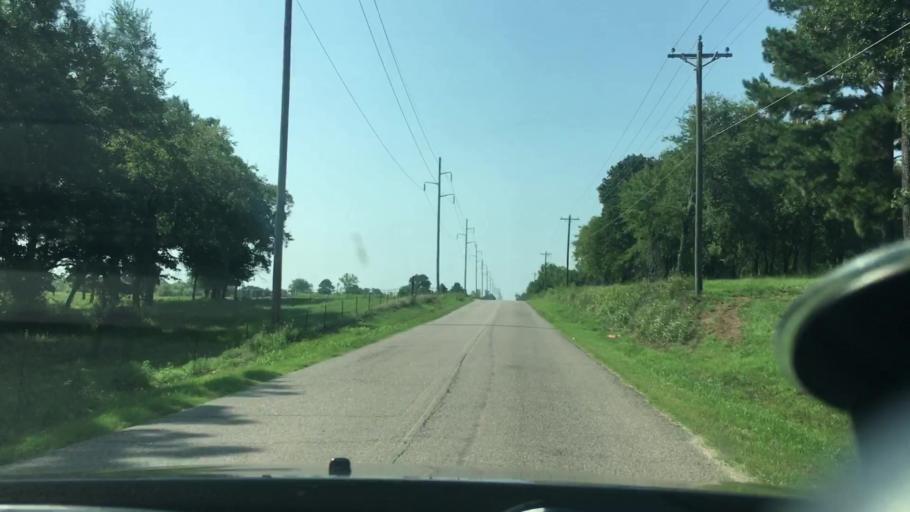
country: US
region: Oklahoma
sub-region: Bryan County
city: Durant
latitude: 34.0168
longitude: -96.4253
